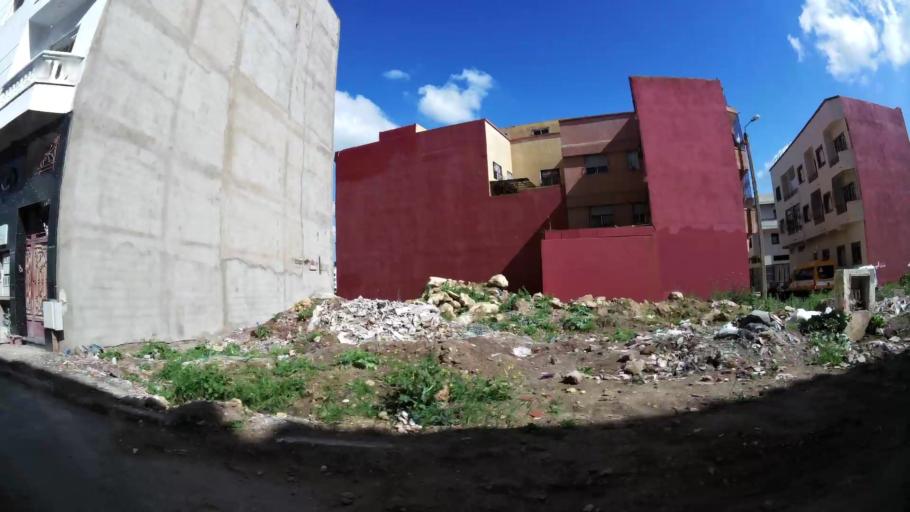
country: MA
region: Grand Casablanca
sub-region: Mediouna
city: Mediouna
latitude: 33.4582
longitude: -7.5125
